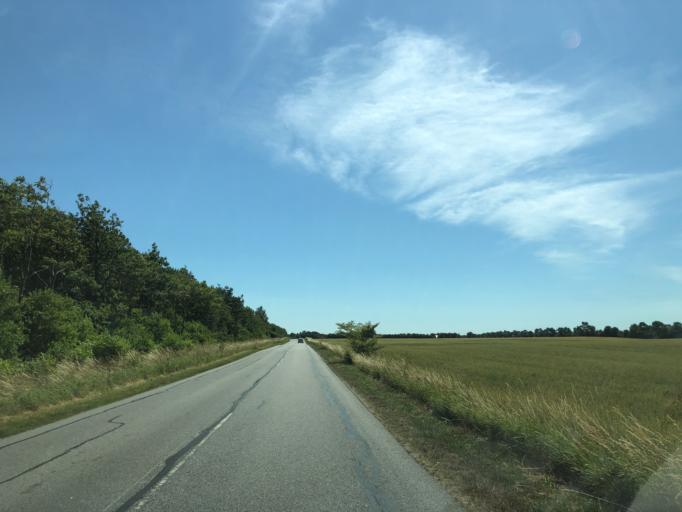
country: DK
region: Central Jutland
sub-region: Skive Kommune
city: Skive
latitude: 56.5057
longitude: 9.0194
